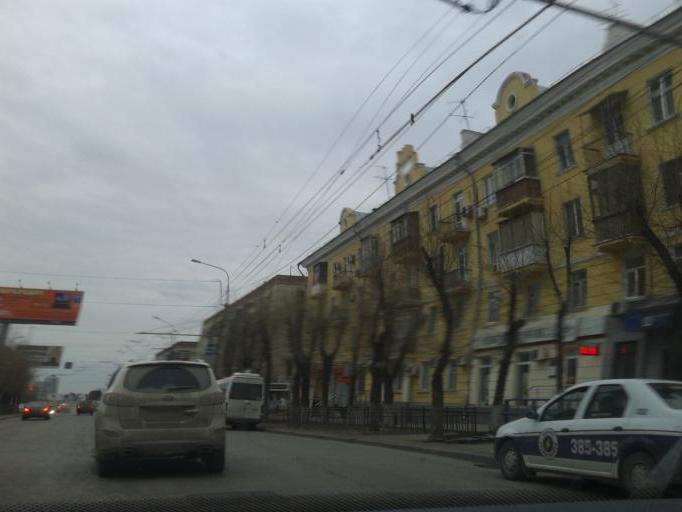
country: RU
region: Volgograd
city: Volgograd
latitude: 48.7170
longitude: 44.5093
